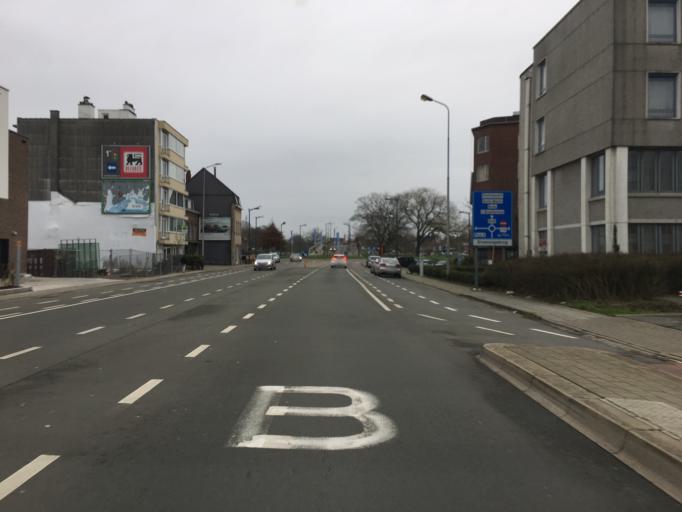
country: BE
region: Flanders
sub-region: Provincie West-Vlaanderen
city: Kortrijk
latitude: 50.8354
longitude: 3.2656
